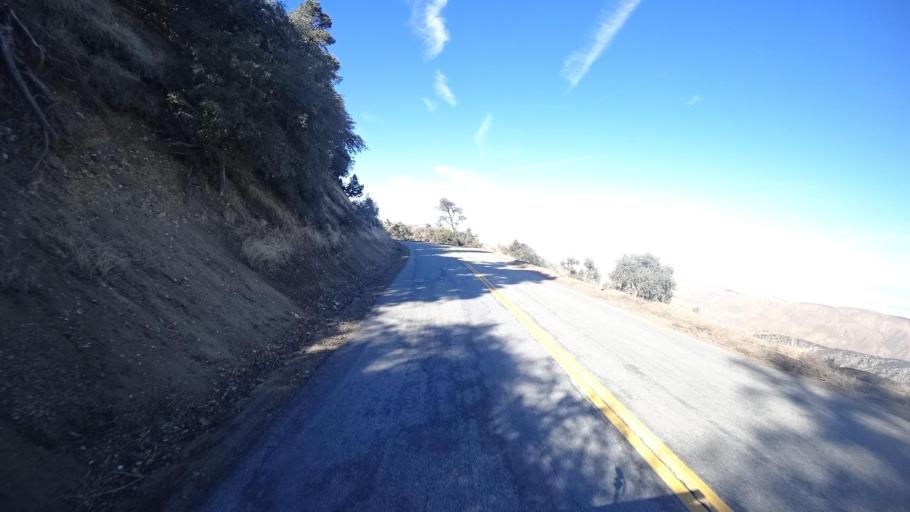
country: US
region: California
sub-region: Kern County
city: Pine Mountain Club
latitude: 34.8787
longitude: -119.3427
